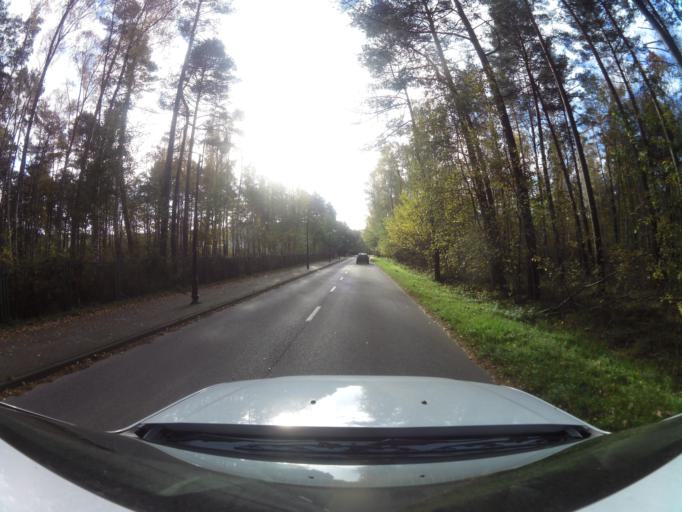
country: PL
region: West Pomeranian Voivodeship
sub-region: Powiat gryficki
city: Cerkwica
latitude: 54.0979
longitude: 15.1215
